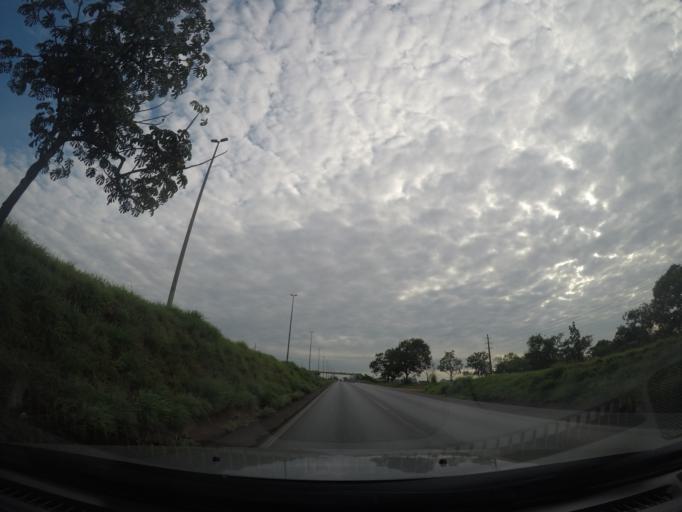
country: BR
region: Goias
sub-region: Planaltina
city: Planaltina
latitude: -15.6048
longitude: -47.6873
